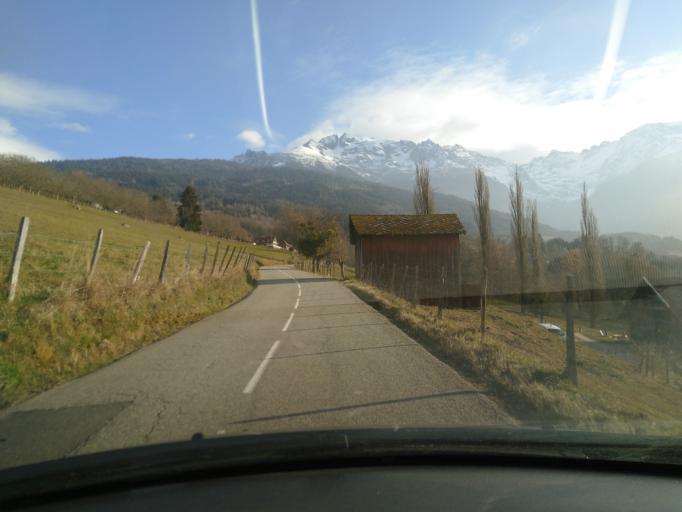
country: FR
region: Rhone-Alpes
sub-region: Departement de l'Isere
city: Villard-Bonnot
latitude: 45.2337
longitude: 5.9286
